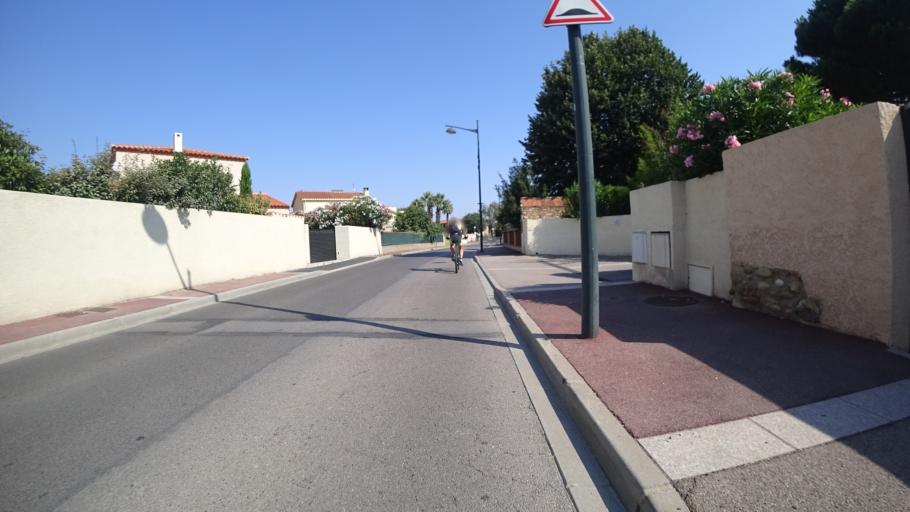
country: FR
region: Languedoc-Roussillon
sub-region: Departement des Pyrenees-Orientales
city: Bompas
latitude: 42.7282
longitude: 2.9321
